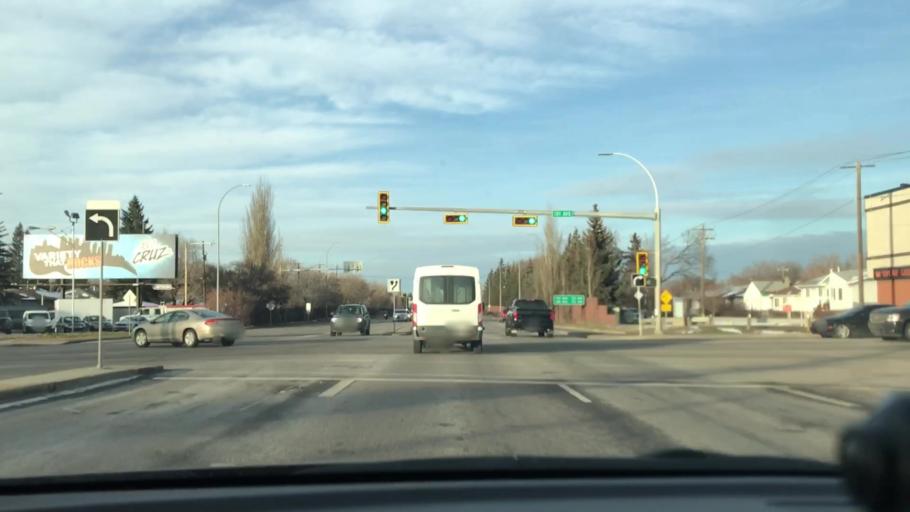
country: CA
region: Alberta
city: Edmonton
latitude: 53.5410
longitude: -113.4434
